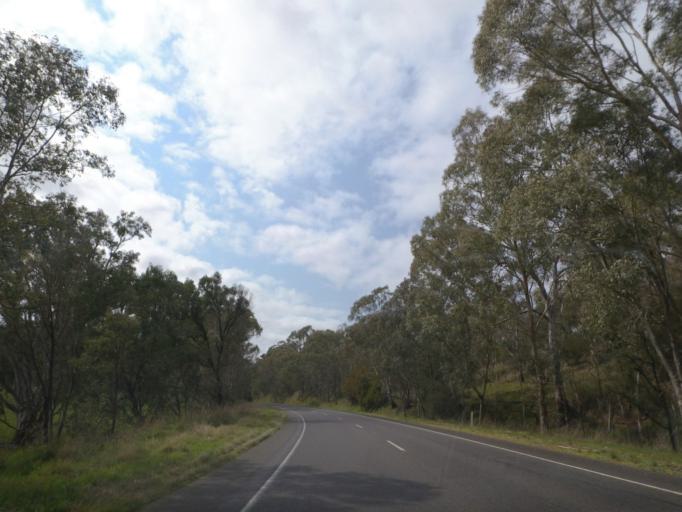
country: AU
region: Victoria
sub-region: Murrindindi
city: Kinglake West
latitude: -37.1433
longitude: 145.2554
